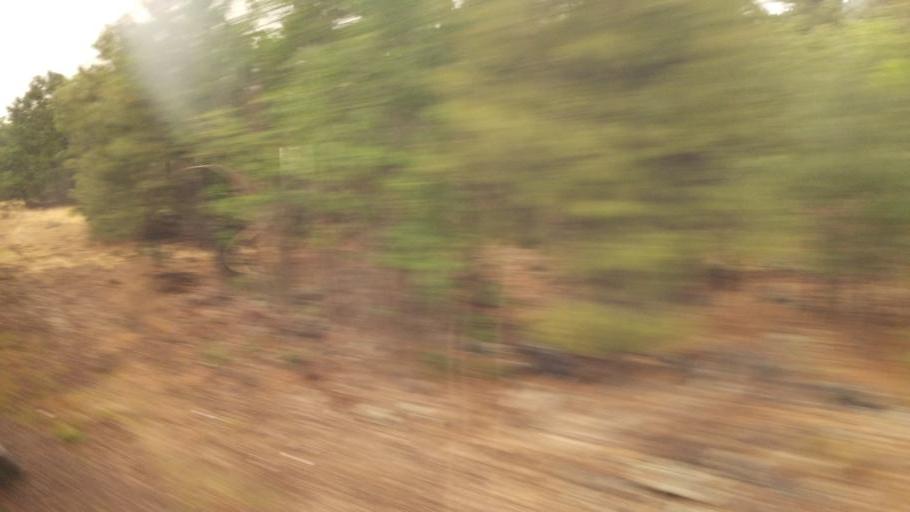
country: US
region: Arizona
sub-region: Coconino County
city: Parks
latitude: 35.2549
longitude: -111.9253
